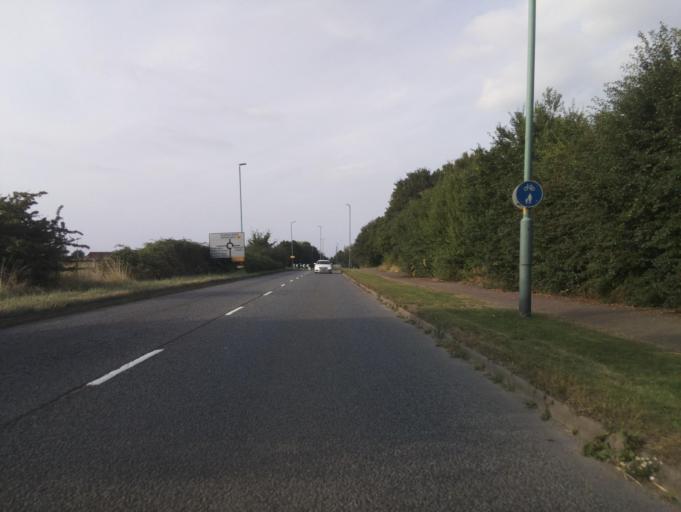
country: GB
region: England
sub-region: Gloucestershire
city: Gotherington
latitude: 51.9445
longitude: -2.0726
